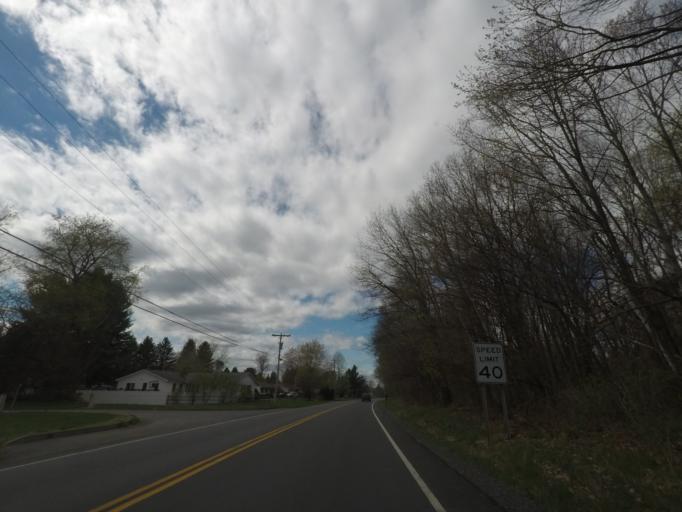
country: US
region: New York
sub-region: Columbia County
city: Valatie
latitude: 42.4031
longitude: -73.6722
